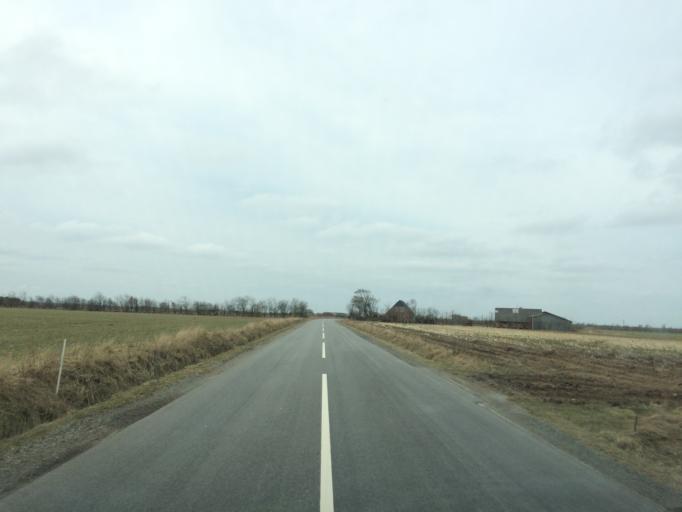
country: DK
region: South Denmark
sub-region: Varde Kommune
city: Oksbol
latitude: 55.7909
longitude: 8.3317
